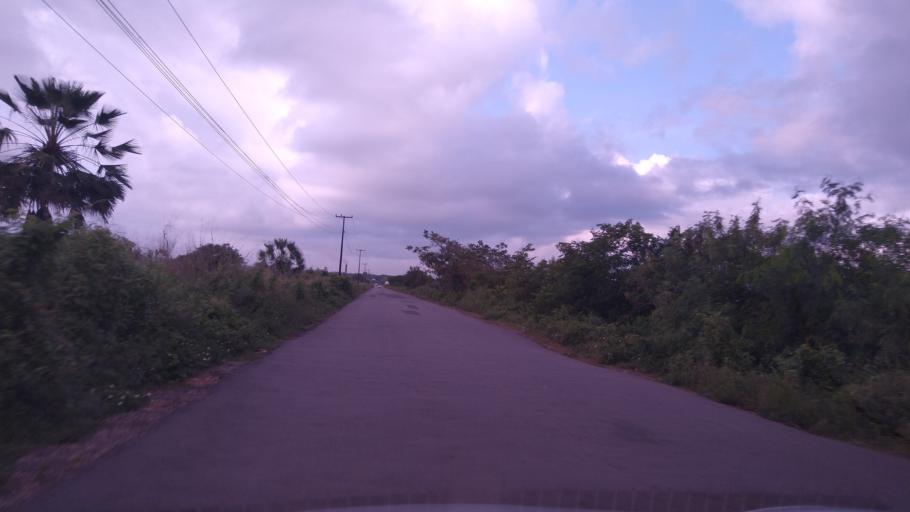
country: BR
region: Ceara
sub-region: Chorozinho
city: Chorozinho
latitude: -4.3057
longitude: -38.4980
